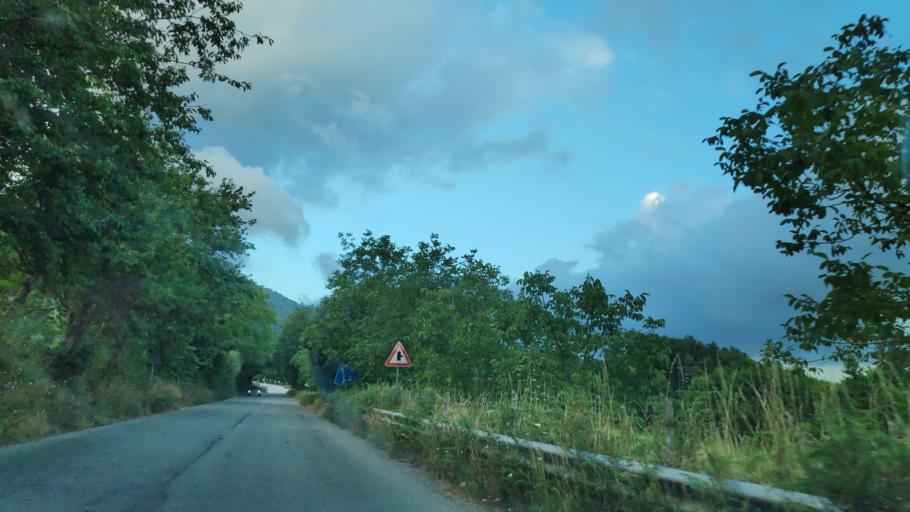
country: IT
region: Calabria
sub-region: Provincia di Vibo-Valentia
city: Mongiana
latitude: 38.5342
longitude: 16.3196
